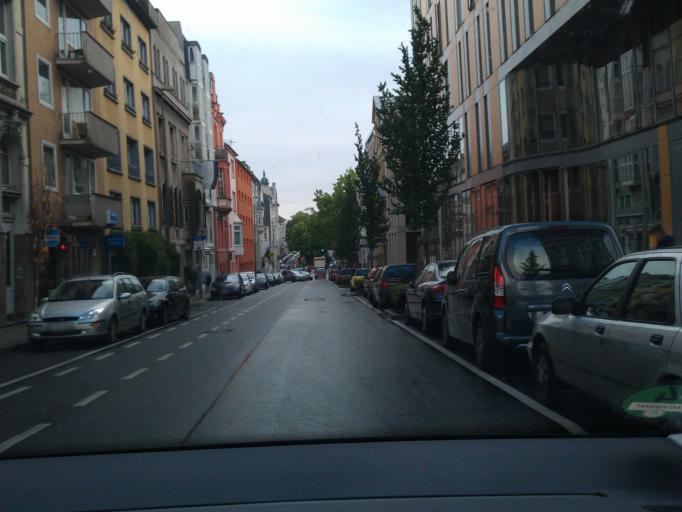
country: DE
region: North Rhine-Westphalia
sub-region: Regierungsbezirk Koln
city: Aachen
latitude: 50.7690
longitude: 6.0975
